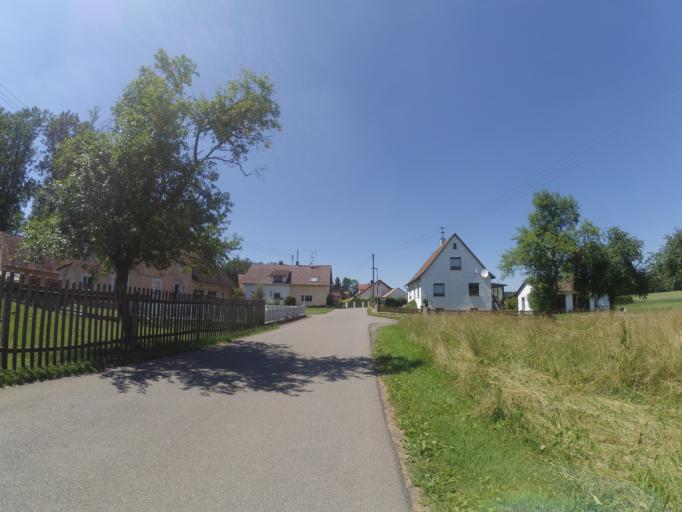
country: DE
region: Baden-Wuerttemberg
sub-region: Tuebingen Region
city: Aulendorf
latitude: 47.9259
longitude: 9.6831
